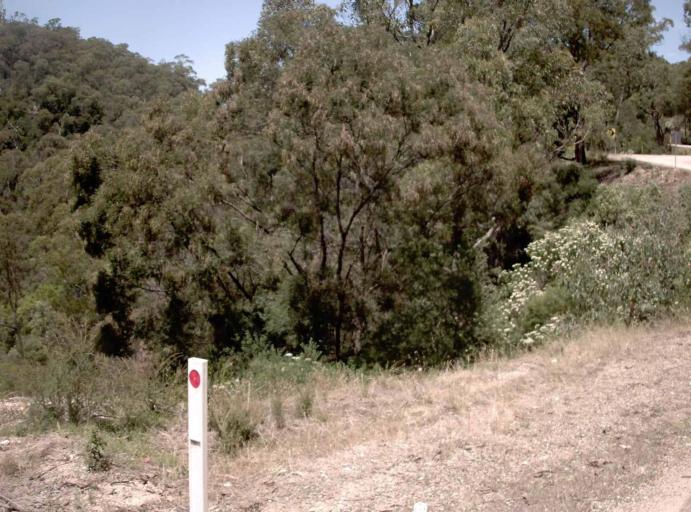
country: AU
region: Victoria
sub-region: East Gippsland
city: Lakes Entrance
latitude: -37.5579
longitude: 147.8864
